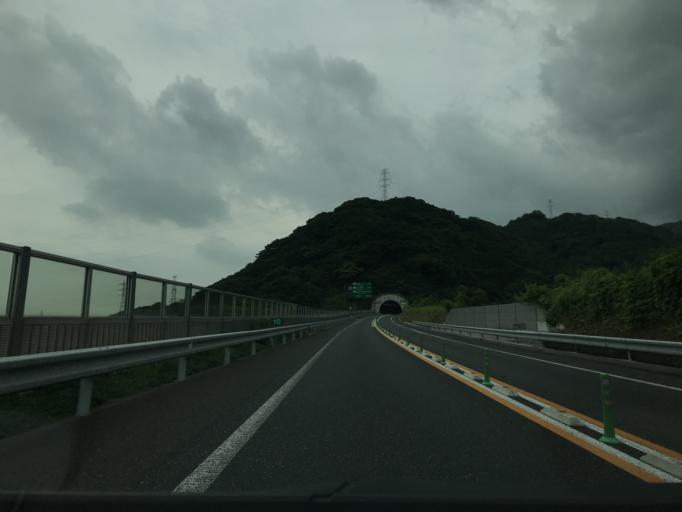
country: JP
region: Fukuoka
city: Kanda
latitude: 33.7799
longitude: 130.9712
